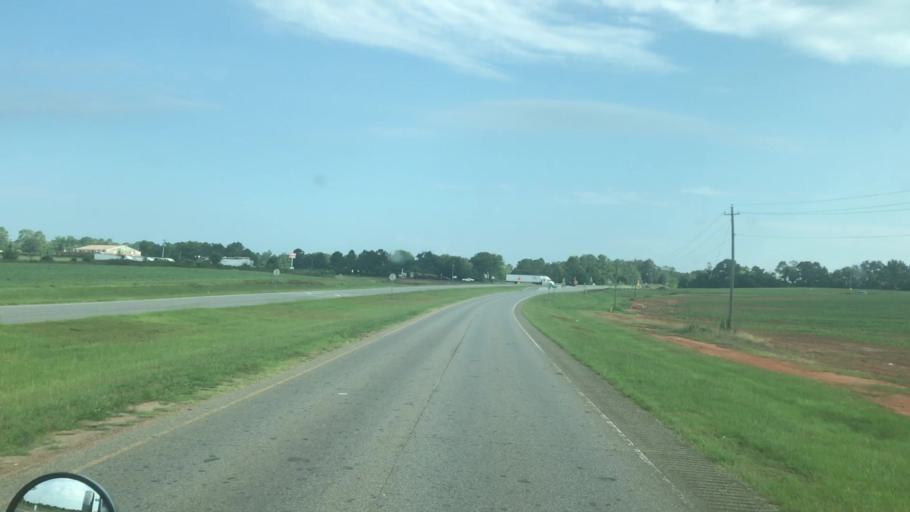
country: US
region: Georgia
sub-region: Early County
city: Blakely
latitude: 31.3883
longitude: -84.9233
